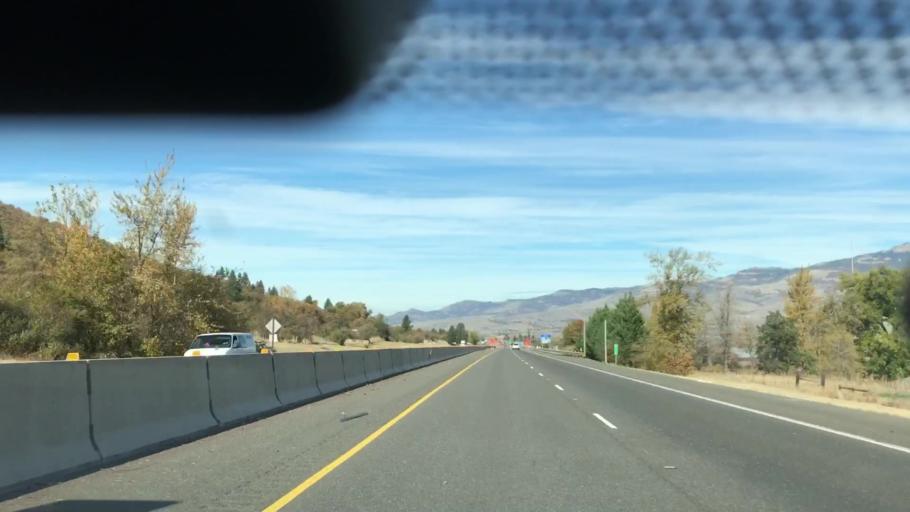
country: US
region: Oregon
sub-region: Jackson County
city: Ashland
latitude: 42.1572
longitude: -122.6472
